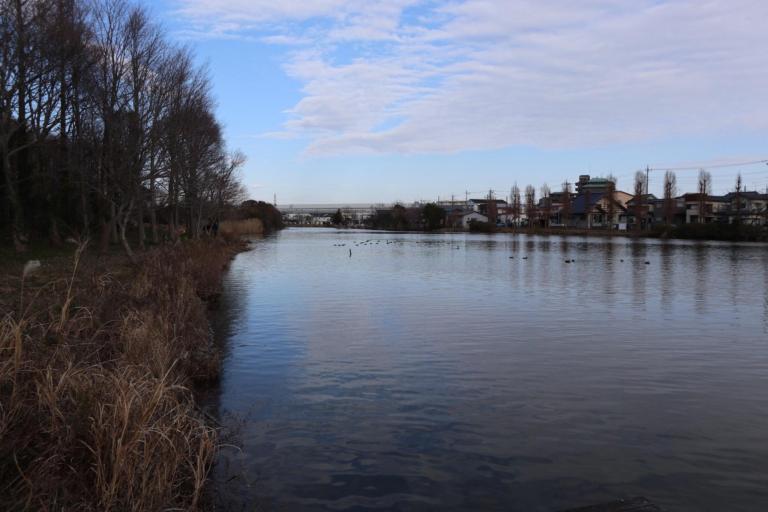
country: JP
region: Chiba
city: Matsudo
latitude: 35.7909
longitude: 139.8731
